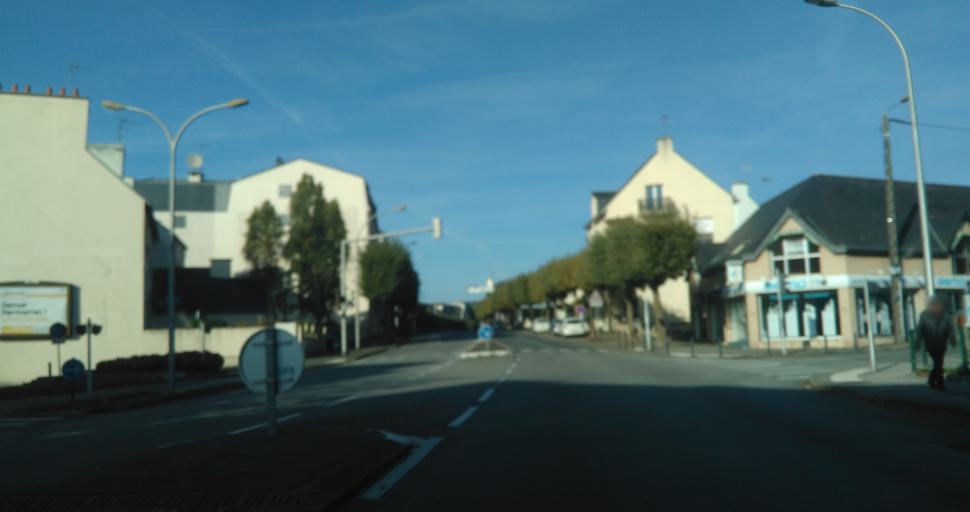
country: FR
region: Brittany
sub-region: Departement du Morbihan
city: Vannes
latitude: 47.6593
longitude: -2.7500
